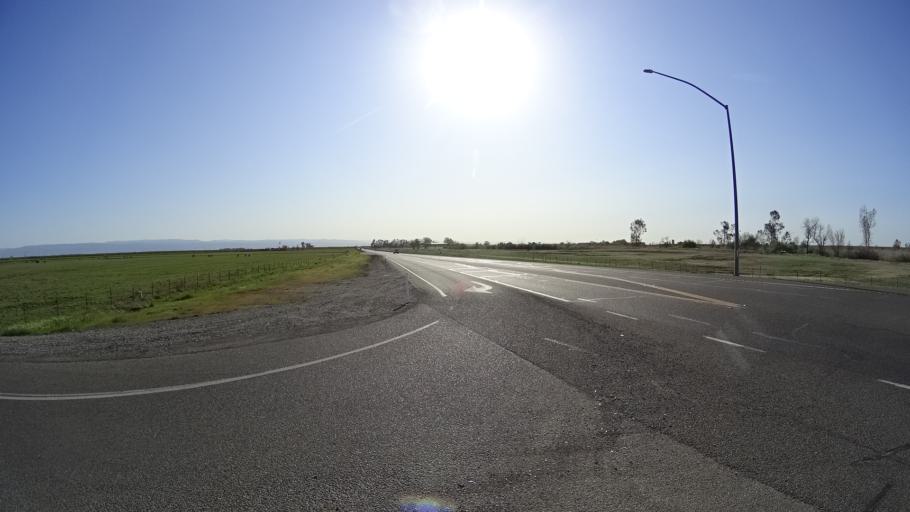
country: US
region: California
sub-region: Glenn County
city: Hamilton City
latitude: 39.7451
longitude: -122.0936
